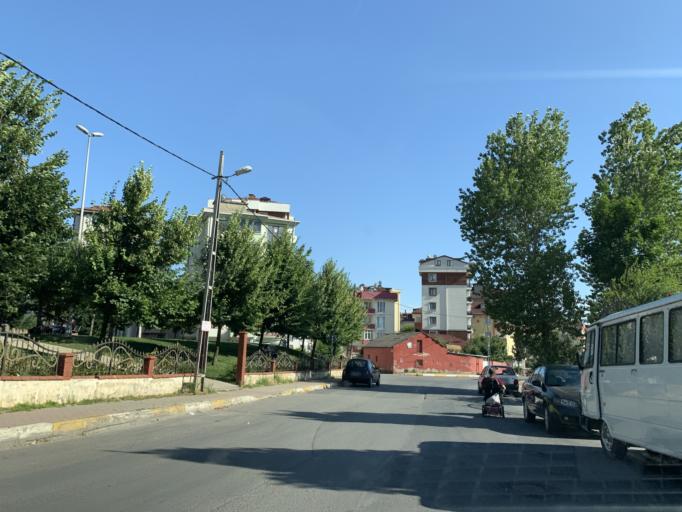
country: TR
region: Istanbul
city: Pendik
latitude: 40.8894
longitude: 29.2689
